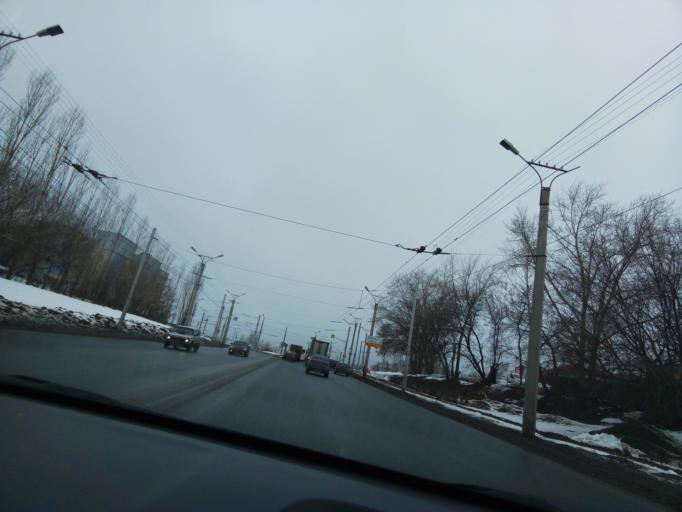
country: RU
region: Chuvashia
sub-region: Cheboksarskiy Rayon
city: Cheboksary
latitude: 56.1268
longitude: 47.2150
